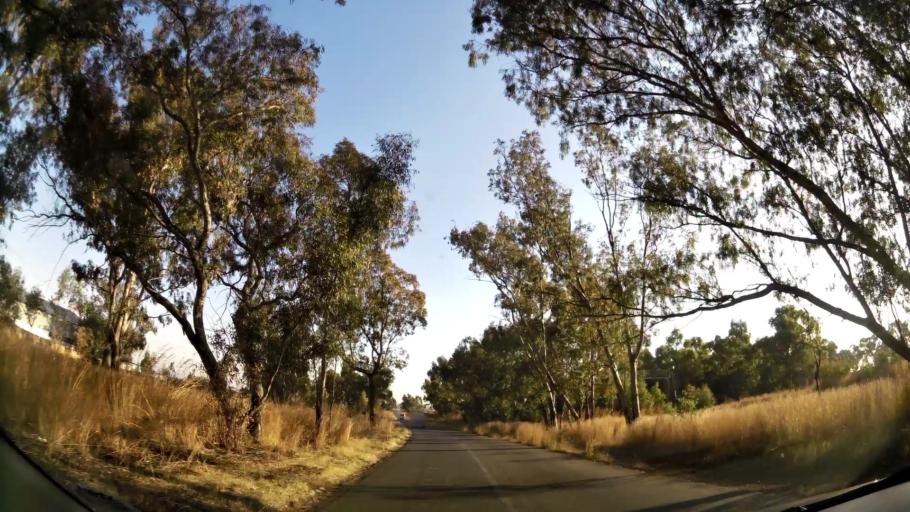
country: ZA
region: Gauteng
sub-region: West Rand District Municipality
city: Randfontein
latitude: -26.1953
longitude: 27.6799
